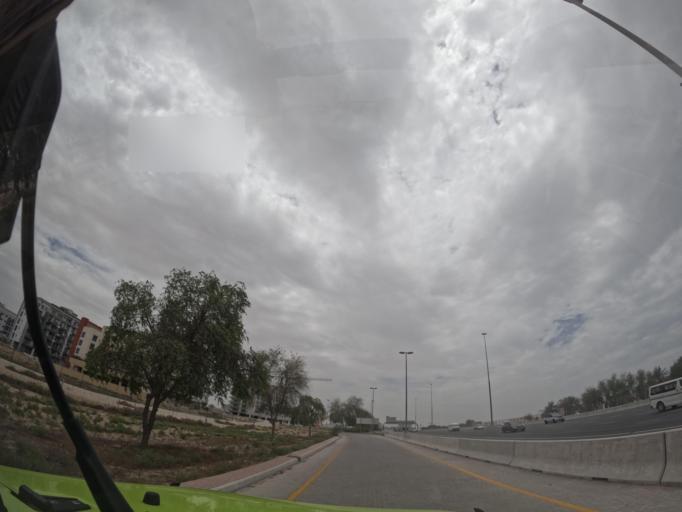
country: AE
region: Ash Shariqah
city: Sharjah
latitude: 25.1505
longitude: 55.3876
